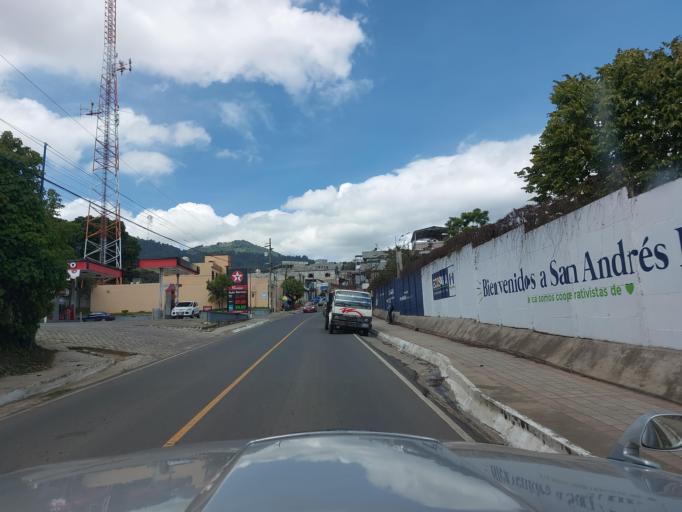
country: GT
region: Chimaltenango
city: San Andres Itzapa
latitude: 14.6228
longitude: -90.8363
